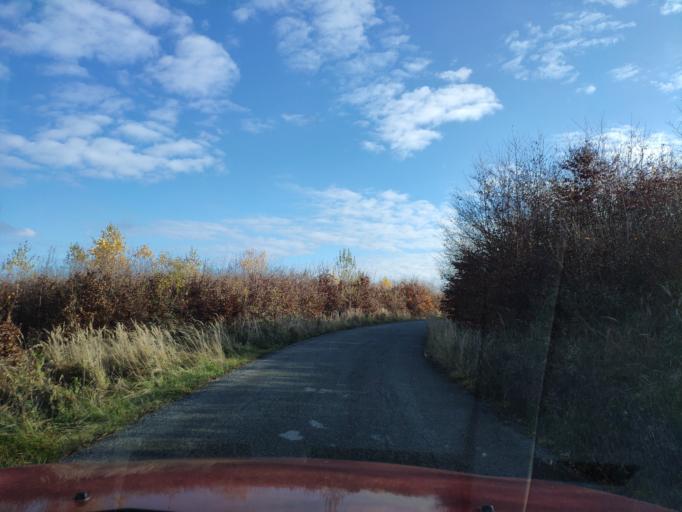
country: SK
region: Kosicky
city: Secovce
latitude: 48.6272
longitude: 21.4570
